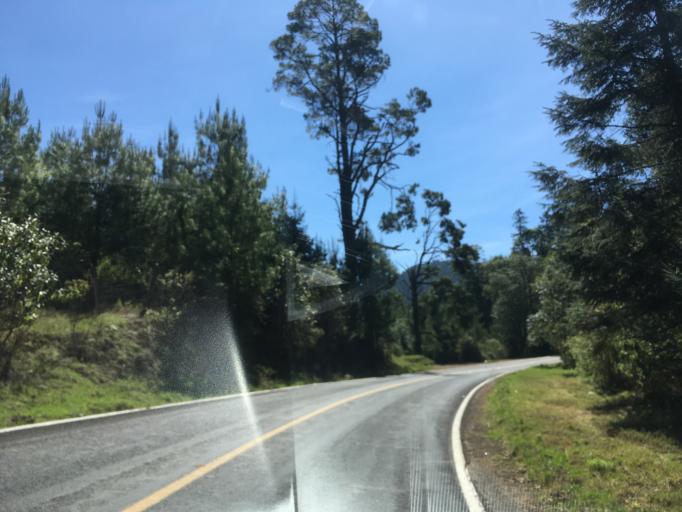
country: MX
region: Michoacan
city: Tzitzio
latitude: 19.6849
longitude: -100.8325
